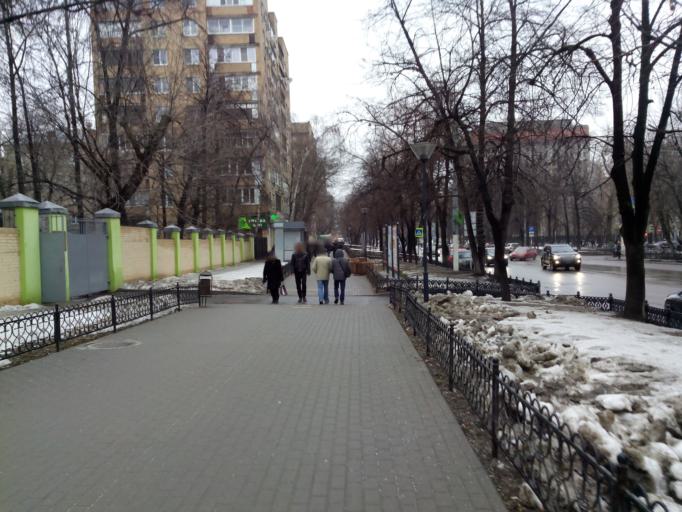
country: RU
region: Moscow
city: Novyye Cheremushki
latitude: 55.7160
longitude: 37.6078
